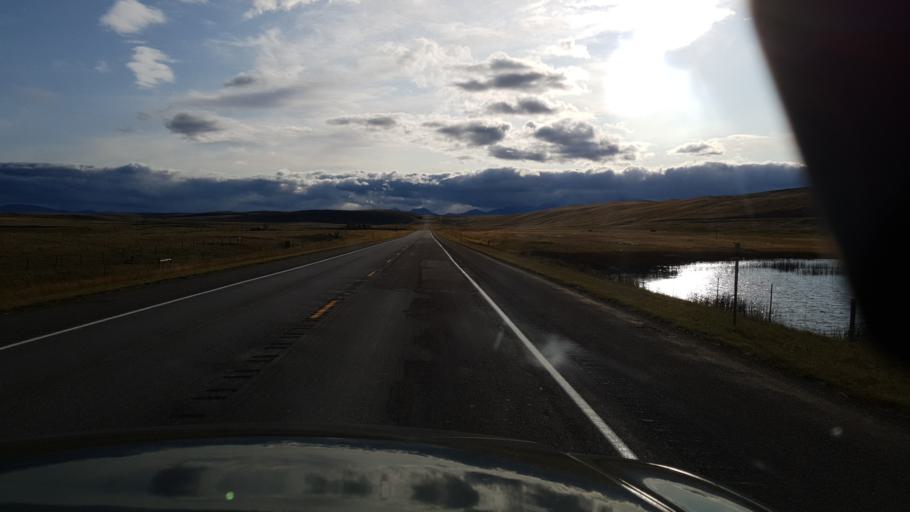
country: US
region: Montana
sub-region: Glacier County
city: South Browning
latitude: 48.5314
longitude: -113.0536
